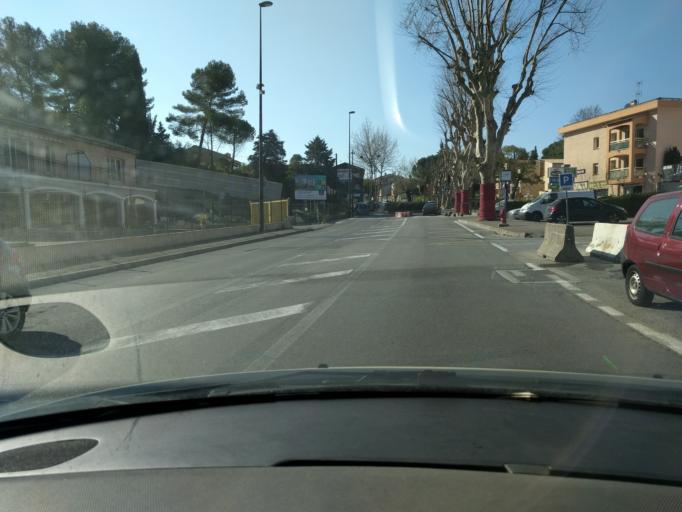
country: FR
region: Provence-Alpes-Cote d'Azur
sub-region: Departement des Alpes-Maritimes
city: Mougins
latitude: 43.6012
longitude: 6.9862
